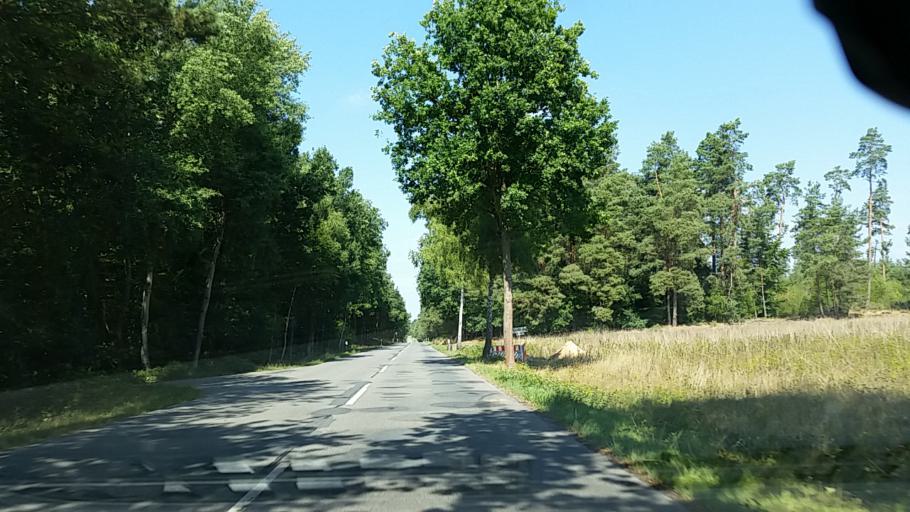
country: DE
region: Lower Saxony
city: Jelmstorf
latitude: 53.1190
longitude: 10.5411
